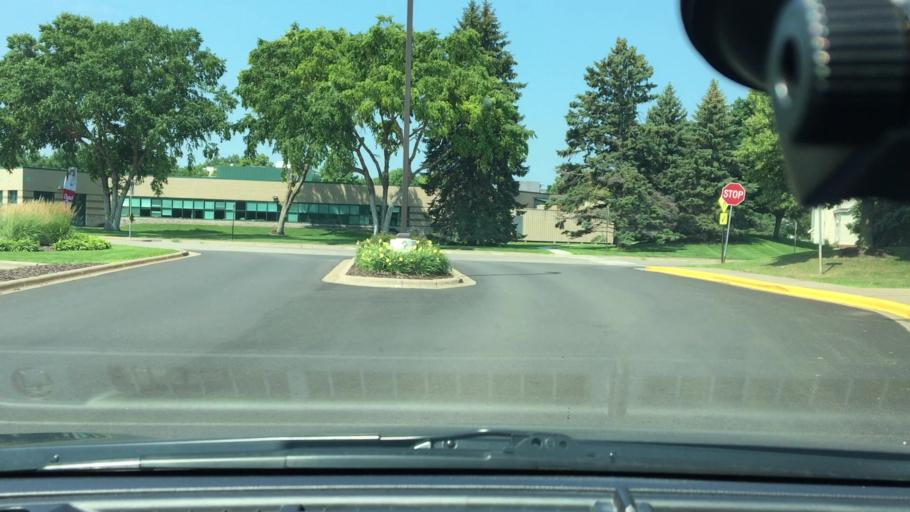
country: US
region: Minnesota
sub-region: Hennepin County
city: Plymouth
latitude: 44.9866
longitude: -93.4102
